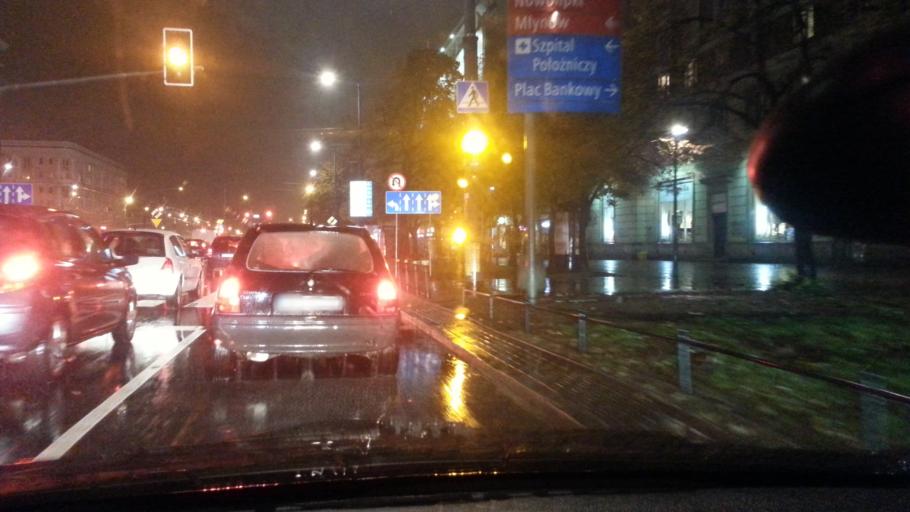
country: PL
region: Masovian Voivodeship
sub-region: Warszawa
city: Wola
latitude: 52.2407
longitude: 20.9950
